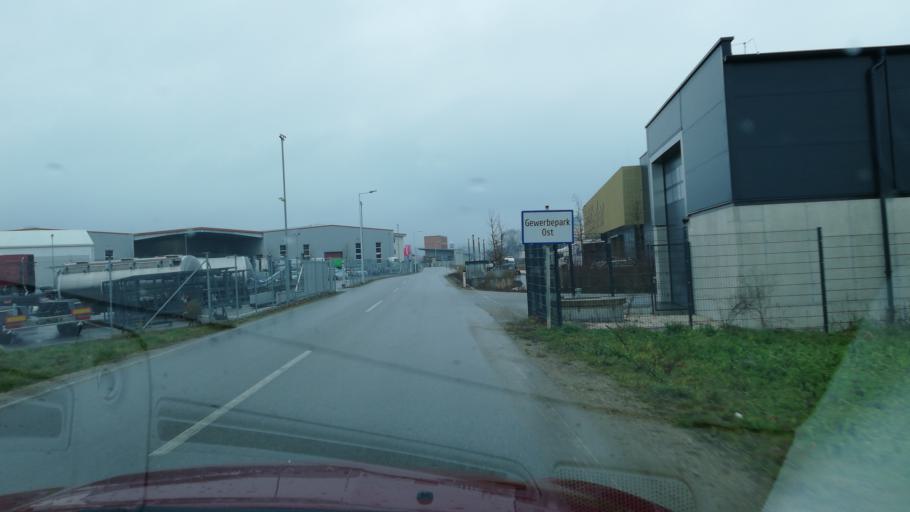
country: AT
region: Upper Austria
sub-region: Politischer Bezirk Vocklabruck
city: Oberndorf bei Schwanenstadt
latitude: 48.0433
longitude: 13.7594
